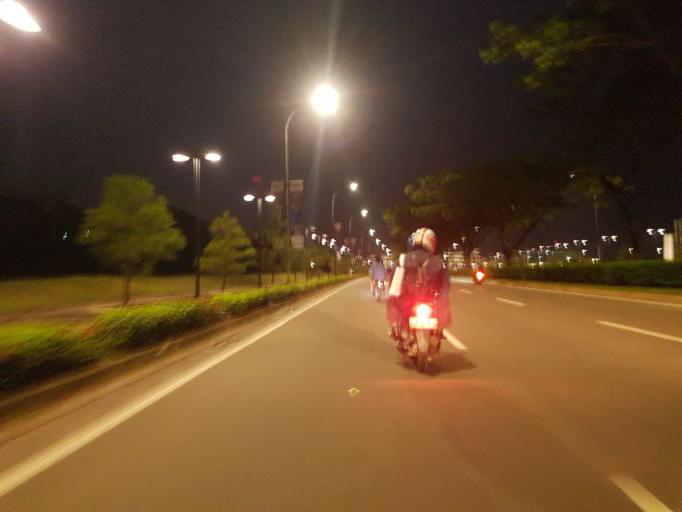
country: ID
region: West Java
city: Serpong
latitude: -6.2990
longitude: 106.6446
